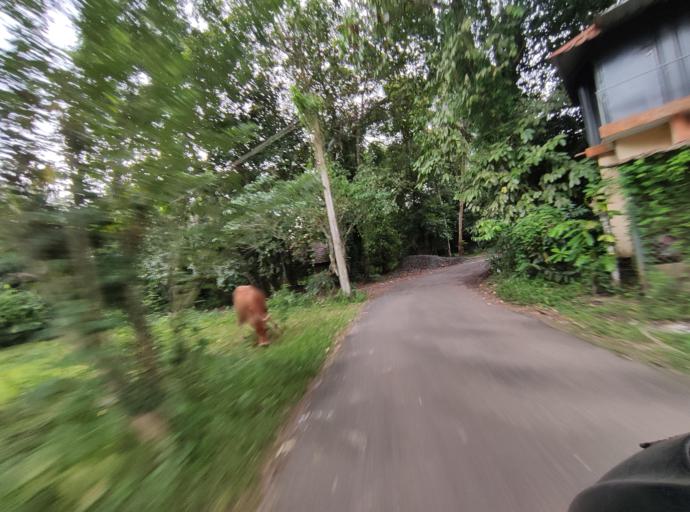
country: IN
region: Kerala
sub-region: Alappuzha
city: Shertallai
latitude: 9.6686
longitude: 76.3483
